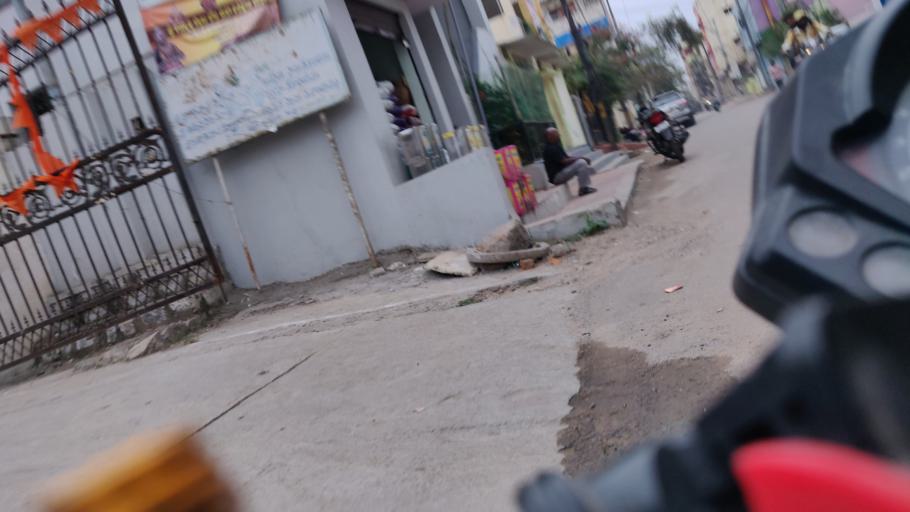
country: IN
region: Telangana
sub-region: Rangareddi
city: Kukatpalli
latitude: 17.4531
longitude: 78.4110
